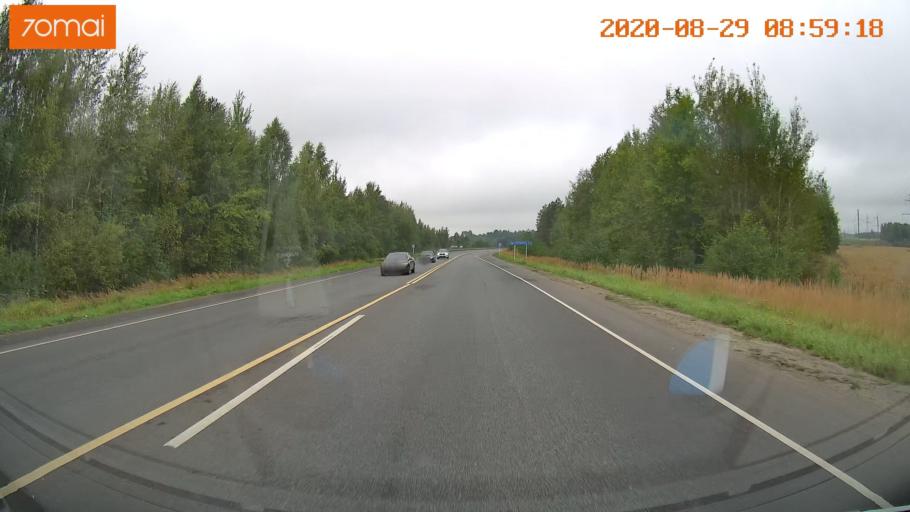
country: RU
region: Ivanovo
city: Staraya Vichuga
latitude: 57.2898
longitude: 41.9079
